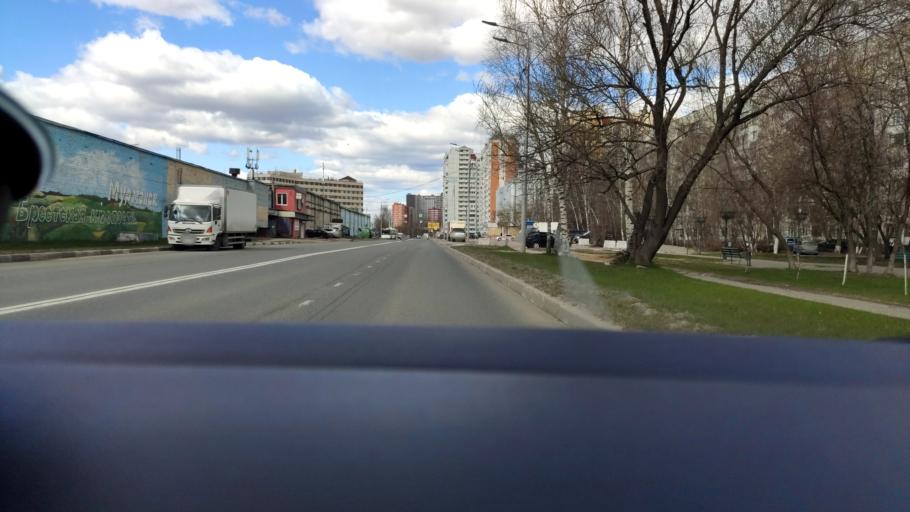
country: RU
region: Moskovskaya
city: Balashikha
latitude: 55.8243
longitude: 37.9542
